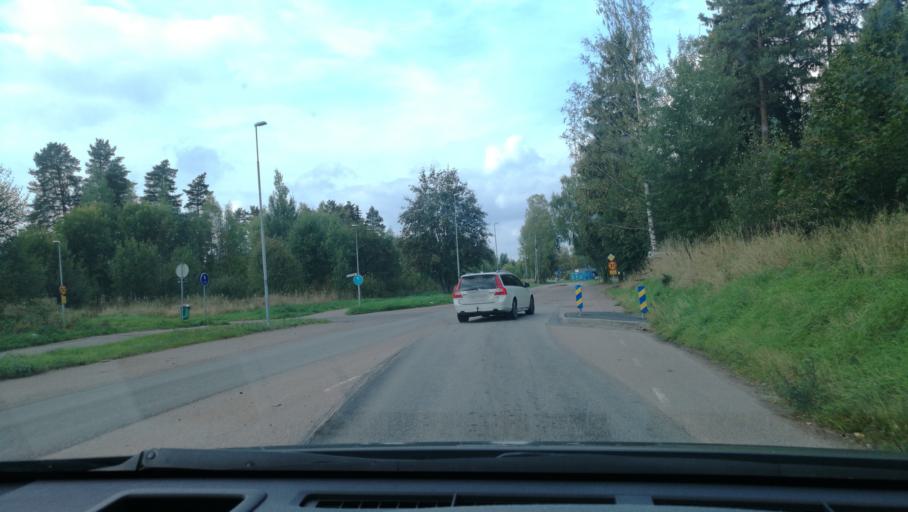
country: SE
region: Dalarna
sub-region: Avesta Kommun
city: Avesta
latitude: 60.1594
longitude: 16.1946
